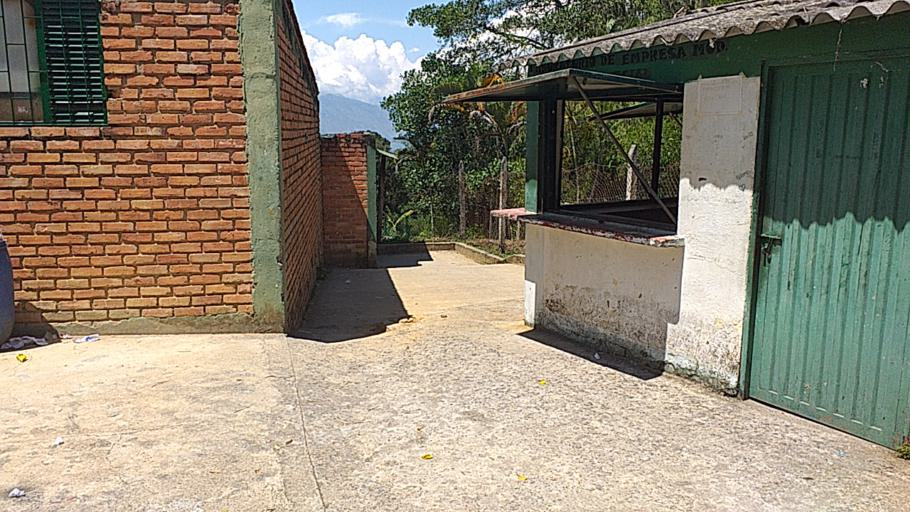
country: CO
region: Boyaca
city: Santana
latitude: 6.0593
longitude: -73.4821
